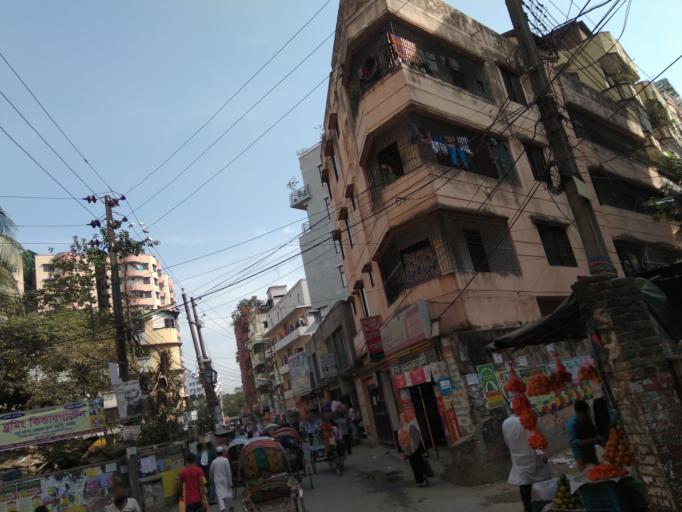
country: BD
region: Dhaka
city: Azimpur
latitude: 23.7733
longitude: 90.3591
